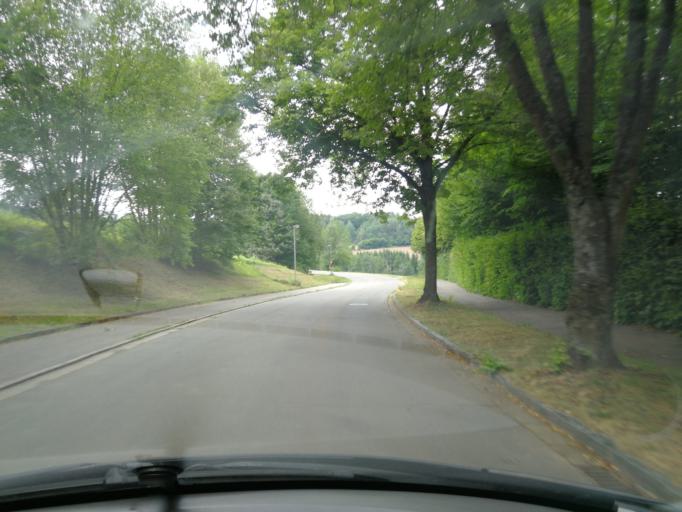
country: DE
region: Bavaria
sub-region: Upper Palatinate
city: Falkenstein
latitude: 49.0979
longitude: 12.4774
